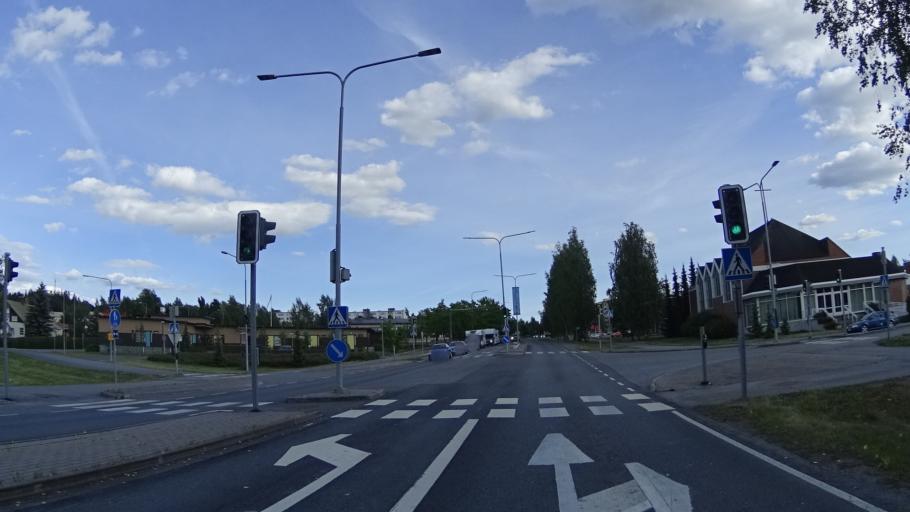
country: FI
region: Haeme
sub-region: Forssa
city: Forssa
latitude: 60.8222
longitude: 23.6295
